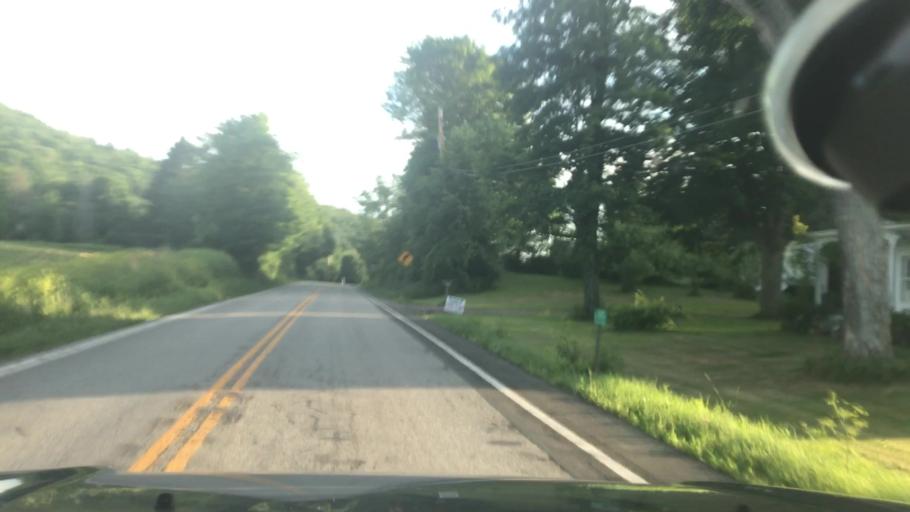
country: US
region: New York
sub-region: Otsego County
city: Unadilla
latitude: 42.3362
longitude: -75.2710
